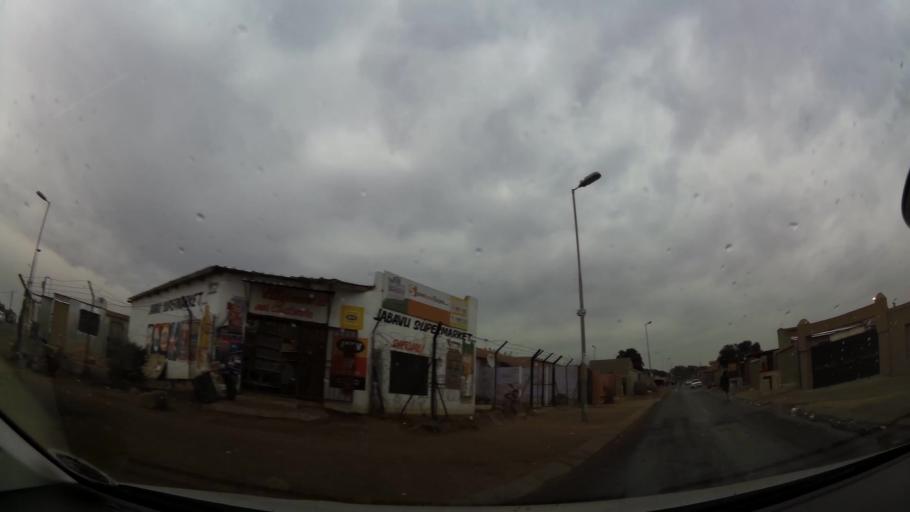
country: ZA
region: Gauteng
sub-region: City of Johannesburg Metropolitan Municipality
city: Soweto
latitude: -26.2479
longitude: 27.8751
